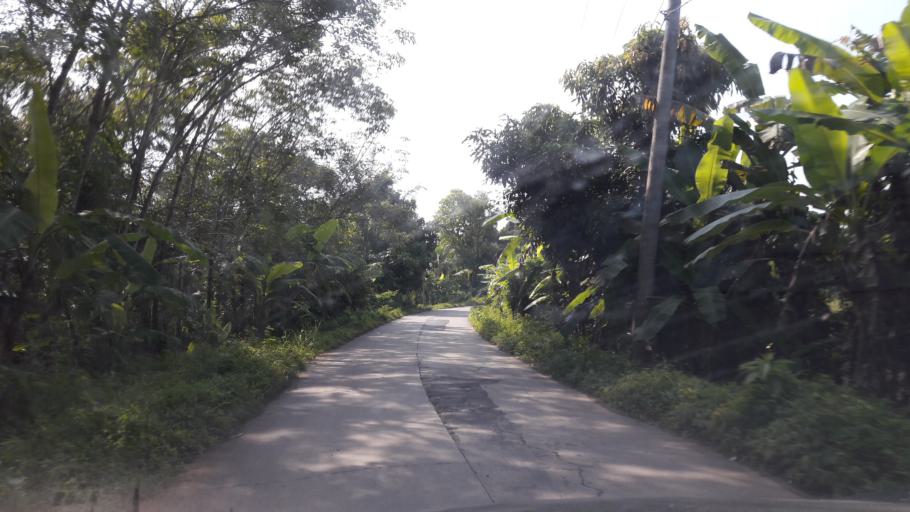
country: ID
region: South Sumatra
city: Prabumulih
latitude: -3.2857
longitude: 104.2178
